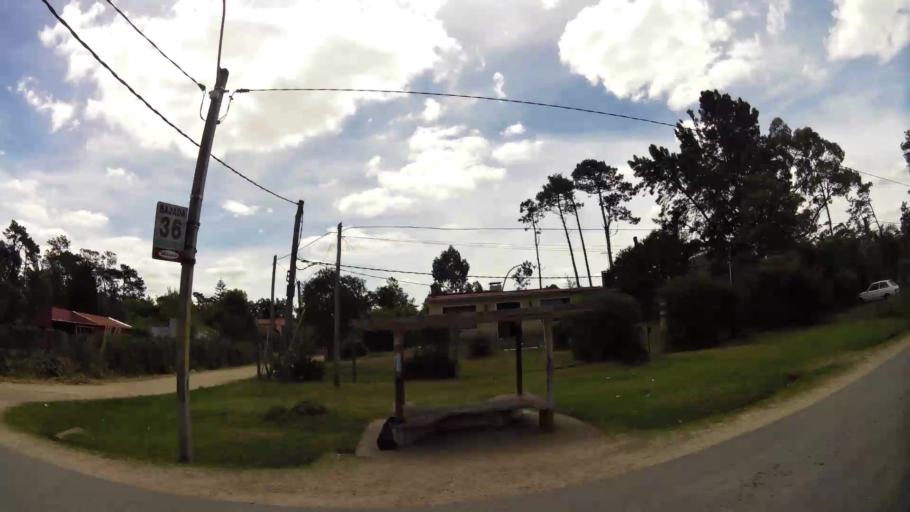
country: UY
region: Canelones
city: Empalme Olmos
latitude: -34.7949
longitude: -55.8842
